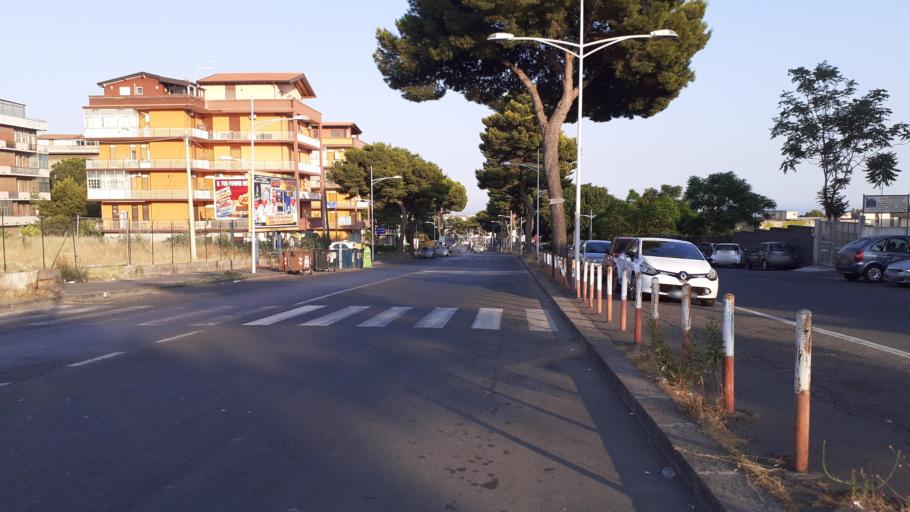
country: IT
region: Sicily
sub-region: Catania
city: Catania
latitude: 37.5062
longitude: 15.0525
